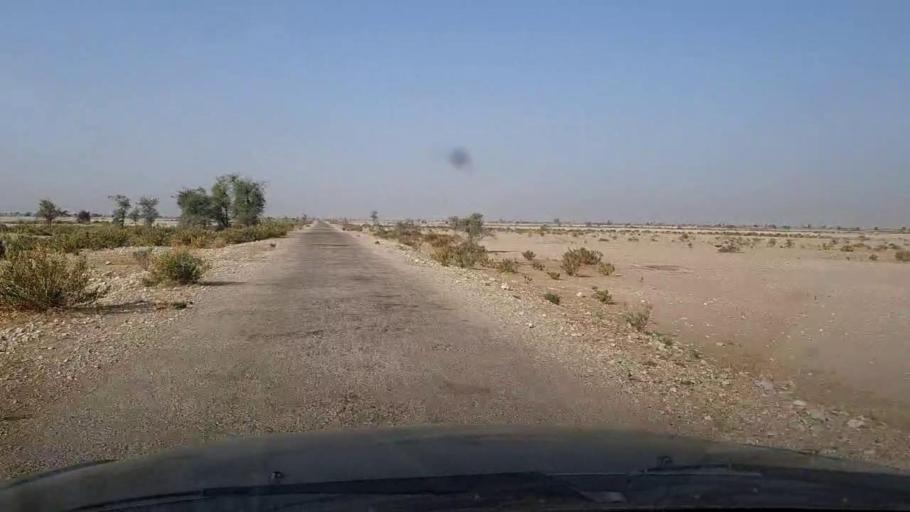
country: PK
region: Sindh
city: Sann
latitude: 25.9902
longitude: 68.0689
